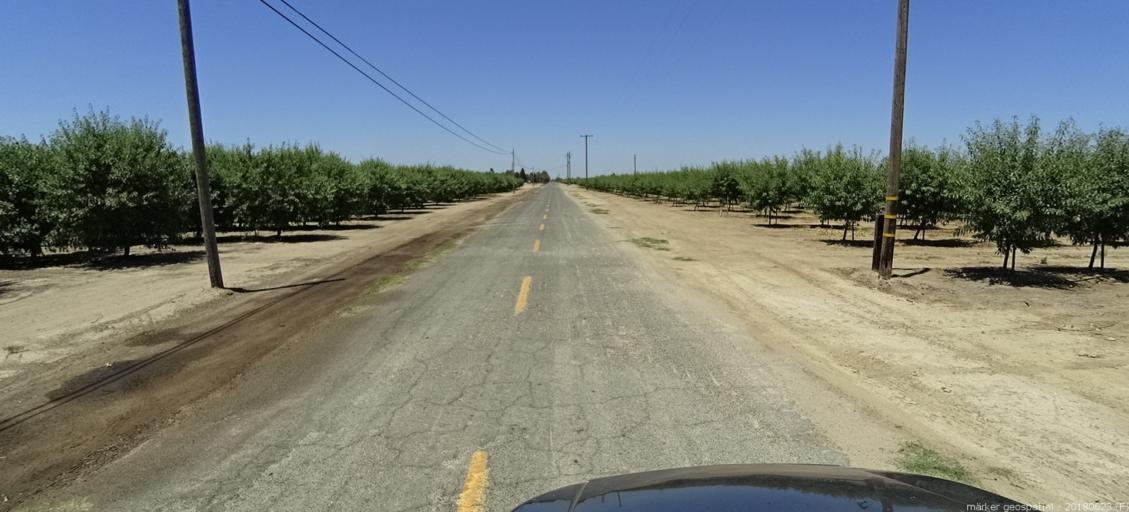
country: US
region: California
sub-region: Madera County
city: Chowchilla
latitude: 37.0909
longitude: -120.2407
